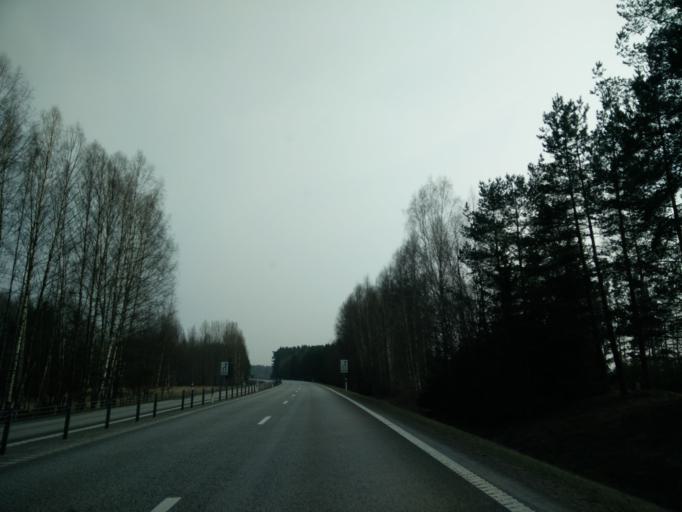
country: SE
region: Vaermland
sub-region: Forshaga Kommun
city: Forshaga
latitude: 59.4765
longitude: 13.4105
